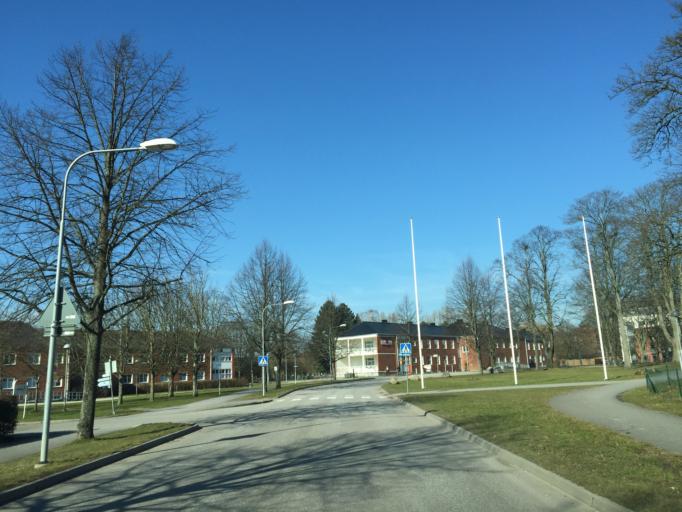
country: SE
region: Skane
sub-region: Lunds Kommun
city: Lund
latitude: 55.6857
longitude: 13.1808
